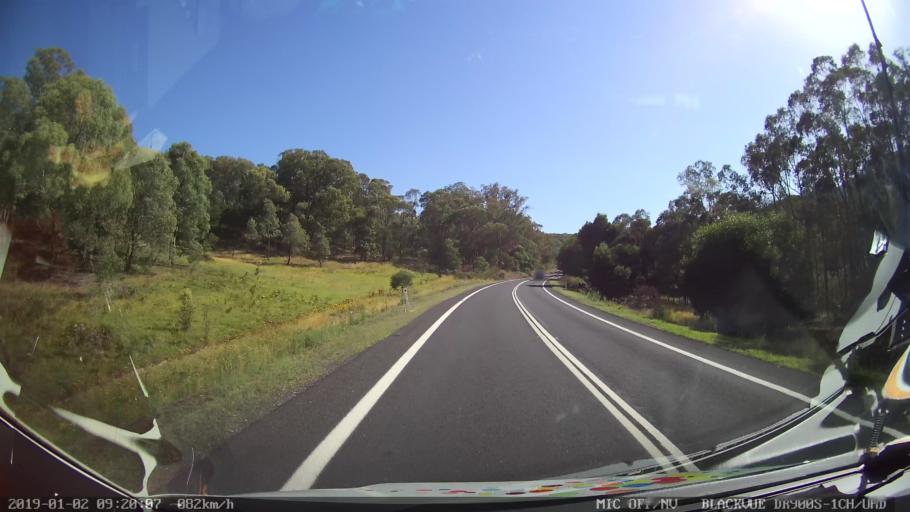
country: AU
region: New South Wales
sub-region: Tumut Shire
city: Tumut
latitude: -35.4151
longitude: 148.2807
